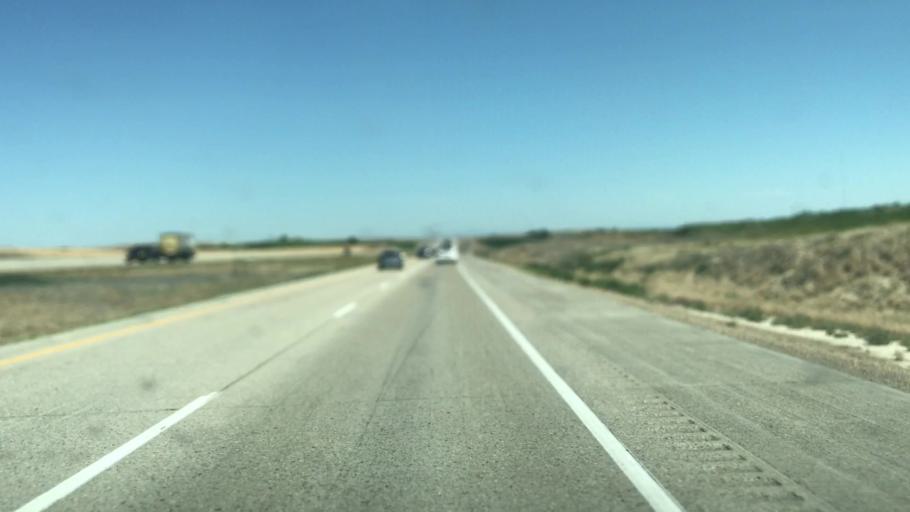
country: US
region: Idaho
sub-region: Payette County
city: New Plymouth
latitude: 43.8309
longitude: -116.7614
